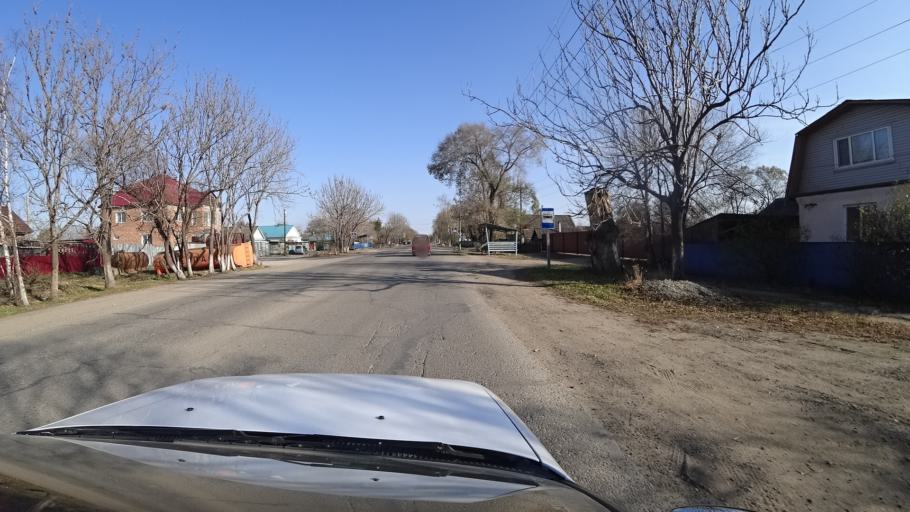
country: RU
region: Primorskiy
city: Dal'nerechensk
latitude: 45.9225
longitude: 133.7484
